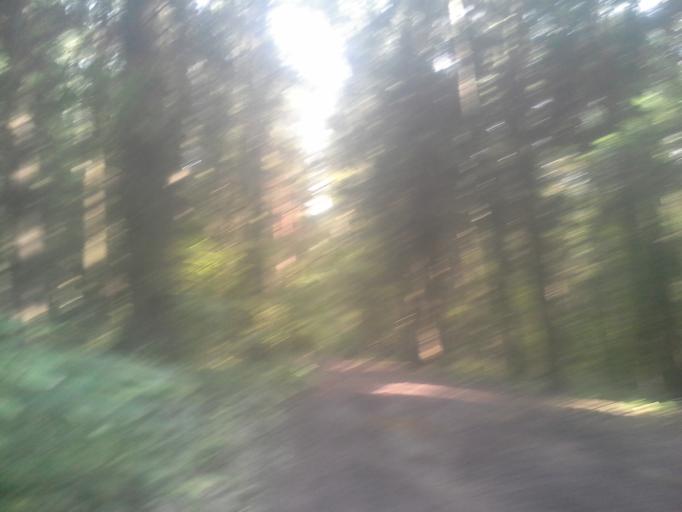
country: RU
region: Moskovskaya
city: Lesnoy Gorodok
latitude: 55.6390
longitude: 37.2424
